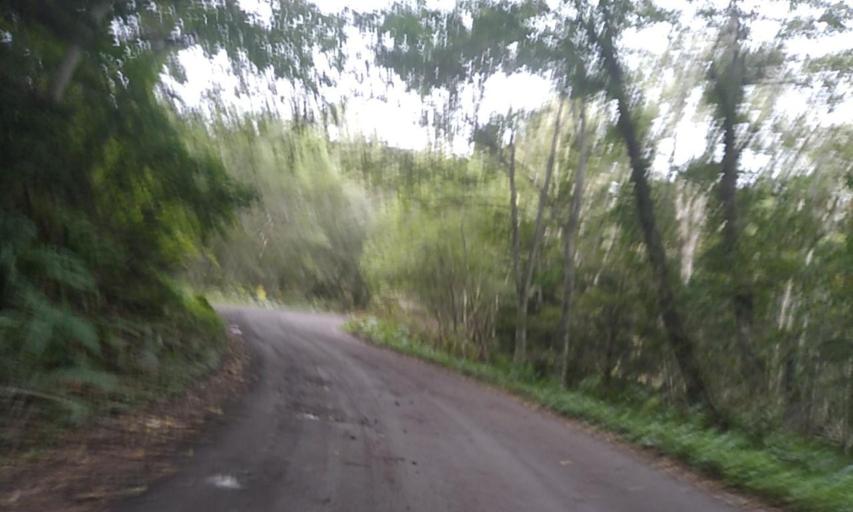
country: JP
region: Hokkaido
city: Abashiri
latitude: 43.6592
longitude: 144.5530
